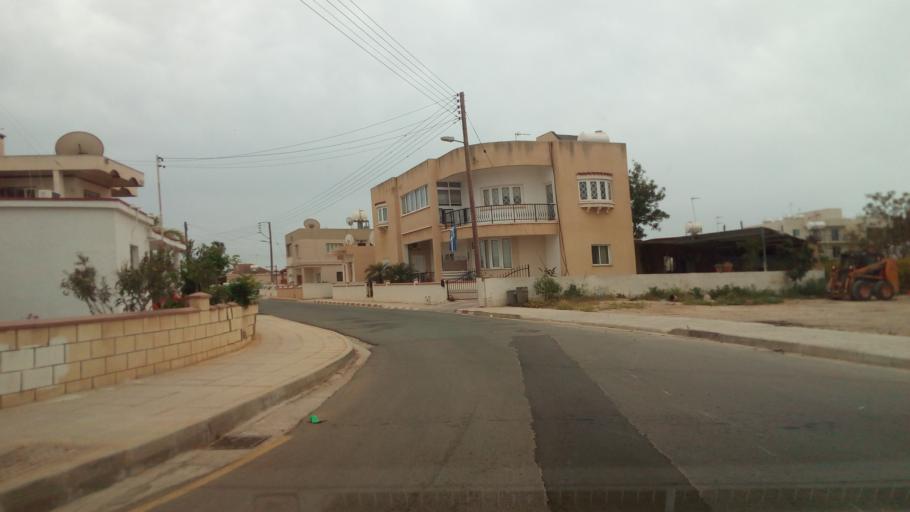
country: CY
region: Ammochostos
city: Liopetri
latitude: 34.9751
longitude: 33.8492
